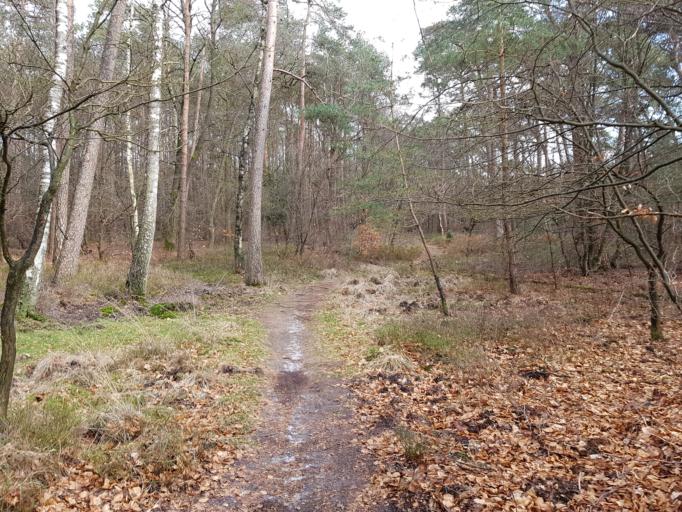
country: NL
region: Gelderland
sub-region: Gemeente Apeldoorn
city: Uddel
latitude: 52.2118
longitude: 5.8654
